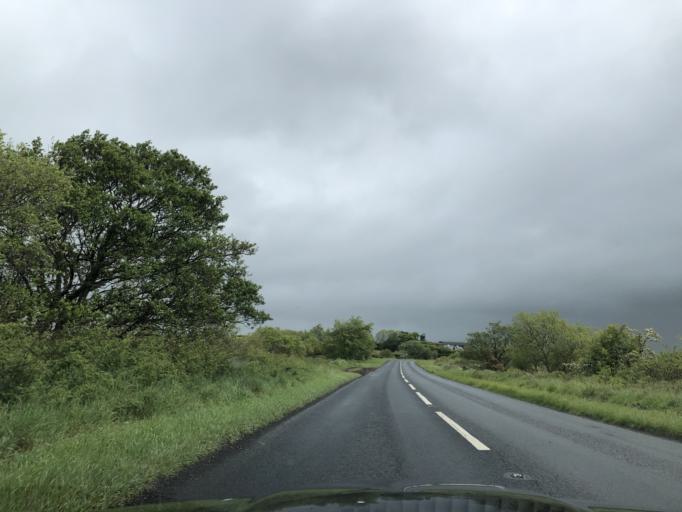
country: GB
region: Northern Ireland
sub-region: Moyle District
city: Ballycastle
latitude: 55.1678
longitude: -6.3586
